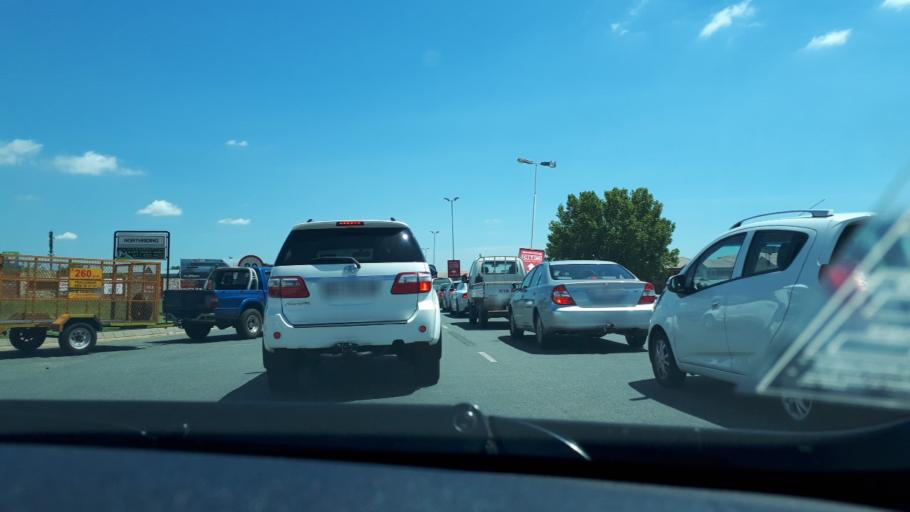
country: ZA
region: Gauteng
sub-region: West Rand District Municipality
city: Muldersdriseloop
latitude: -26.0486
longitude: 27.9565
